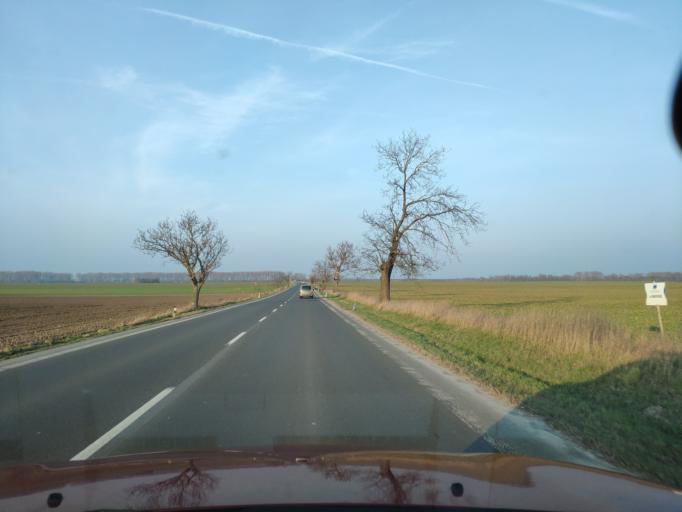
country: SK
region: Trnavsky
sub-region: Okres Trnava
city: Trnava
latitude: 48.3177
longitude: 17.5097
